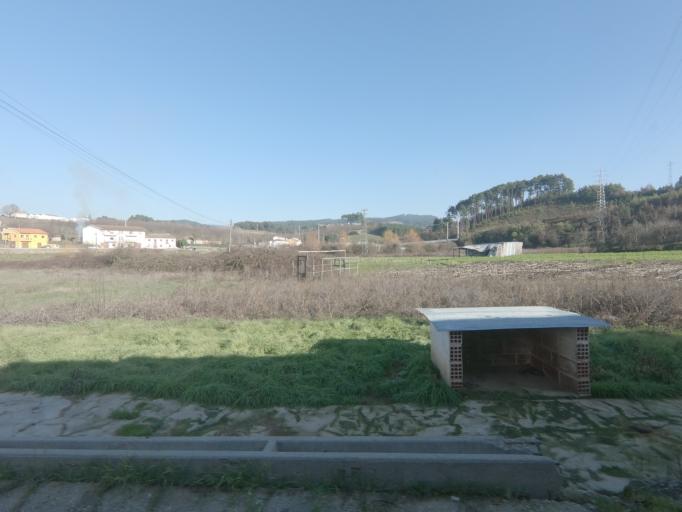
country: PT
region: Vila Real
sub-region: Vila Real
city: Vila Real
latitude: 41.2893
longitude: -7.7255
